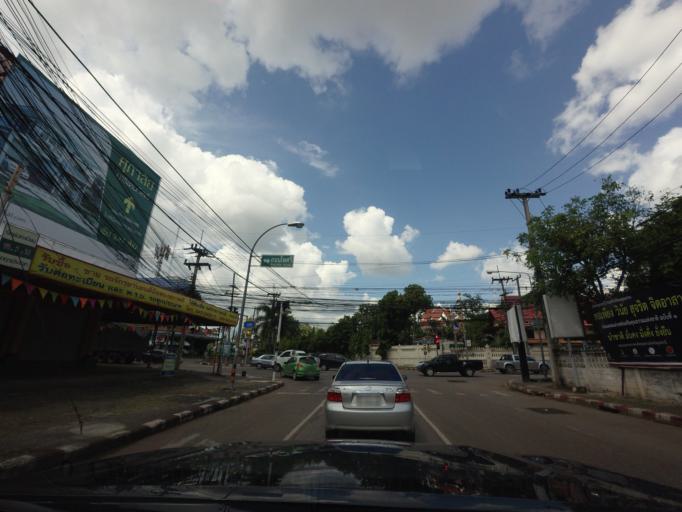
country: TH
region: Changwat Udon Thani
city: Udon Thani
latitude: 17.4132
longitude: 102.7771
